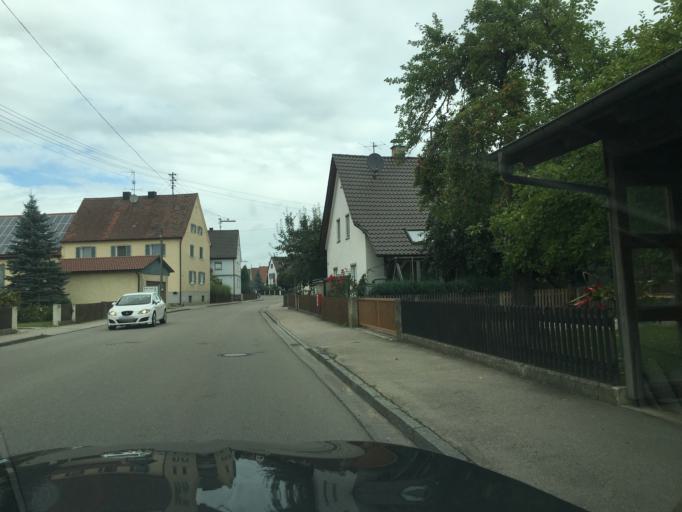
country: DE
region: Bavaria
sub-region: Swabia
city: Altenmunster
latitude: 48.4653
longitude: 10.5904
